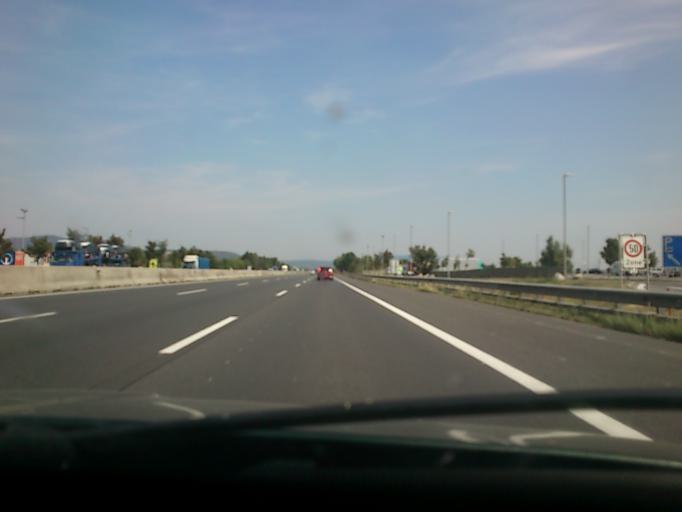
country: AT
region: Lower Austria
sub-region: Politischer Bezirk Baden
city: Leobersdorf
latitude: 47.9082
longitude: 16.2080
